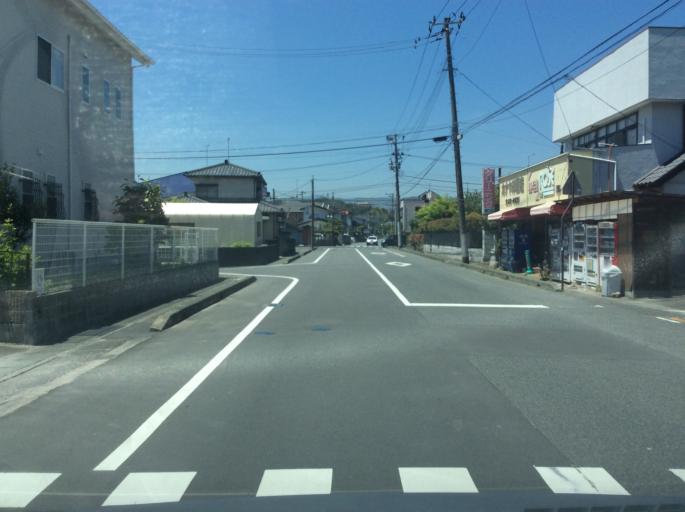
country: JP
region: Fukushima
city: Iwaki
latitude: 37.0767
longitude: 140.8822
